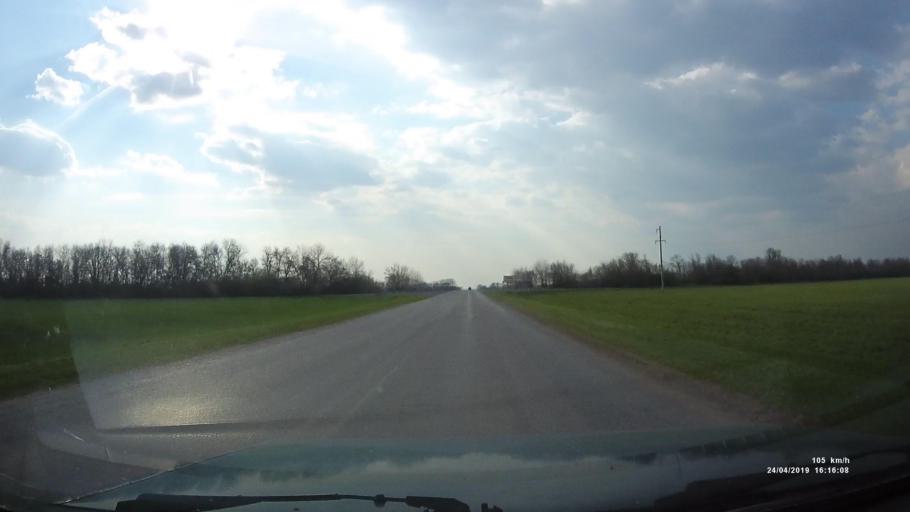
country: RU
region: Rostov
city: Sovetskoye
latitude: 46.7615
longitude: 42.1660
